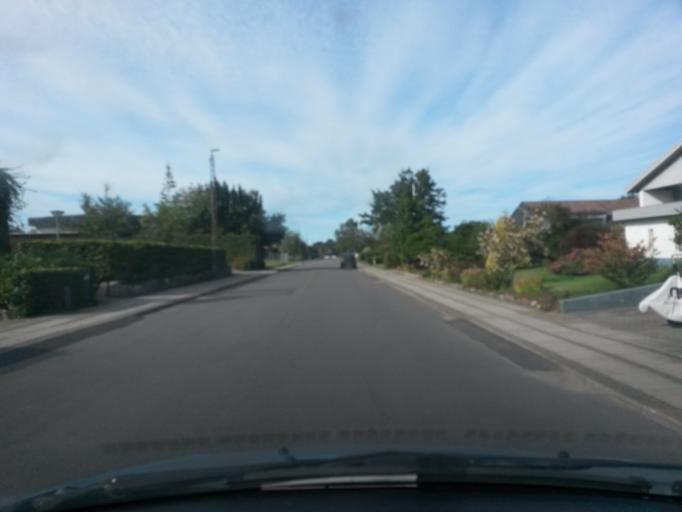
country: DK
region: Central Jutland
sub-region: Silkeborg Kommune
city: Kjellerup
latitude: 56.2797
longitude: 9.4370
